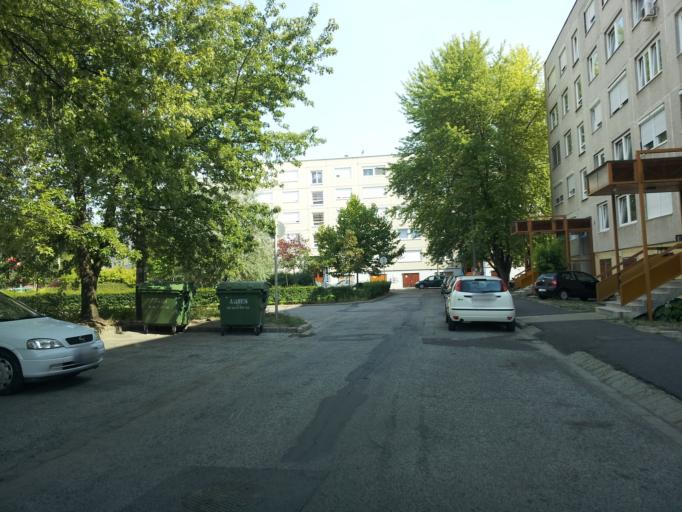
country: HU
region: Pest
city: Szigetszentmiklos
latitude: 47.3403
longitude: 19.0306
